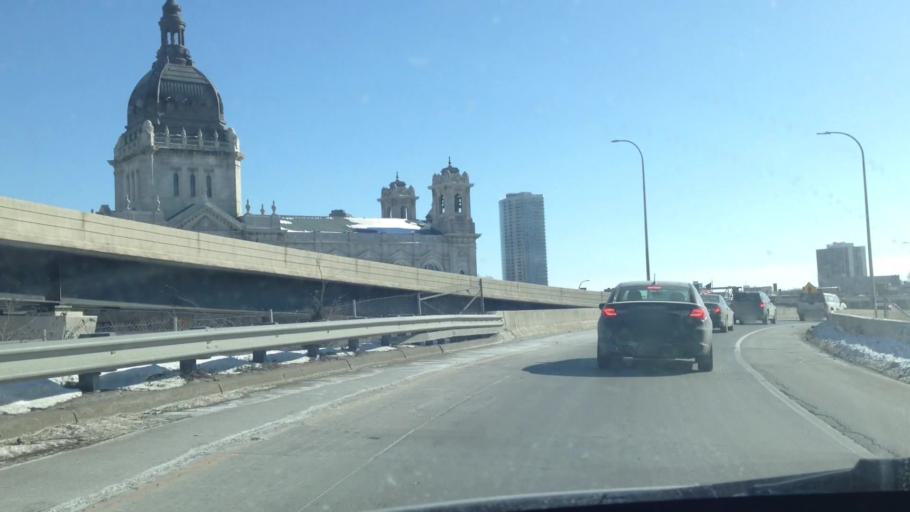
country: US
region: Minnesota
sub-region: Hennepin County
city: Minneapolis
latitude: 44.9739
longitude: -93.2885
